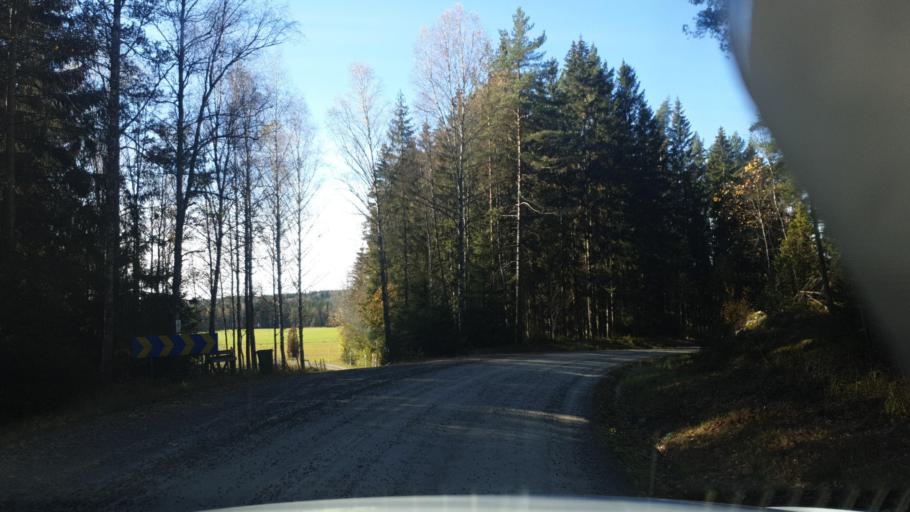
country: SE
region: Vaermland
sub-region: Karlstads Kommun
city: Edsvalla
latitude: 59.4863
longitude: 13.0529
